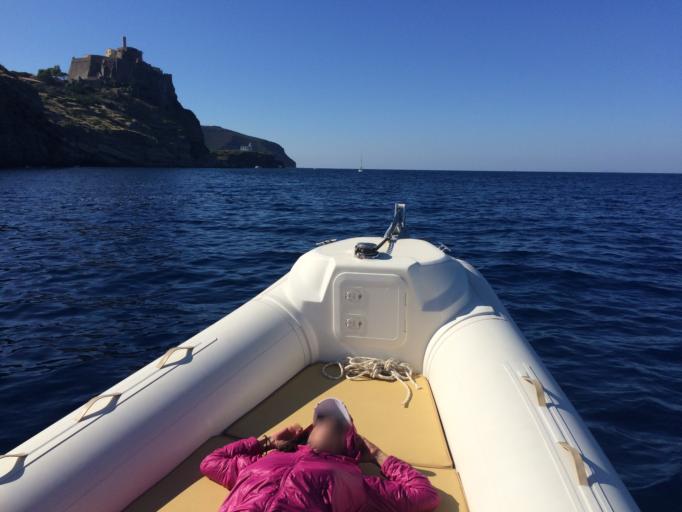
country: IT
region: Tuscany
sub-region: Provincia di Livorno
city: Capraia Isola
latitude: 43.0442
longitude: 9.8494
